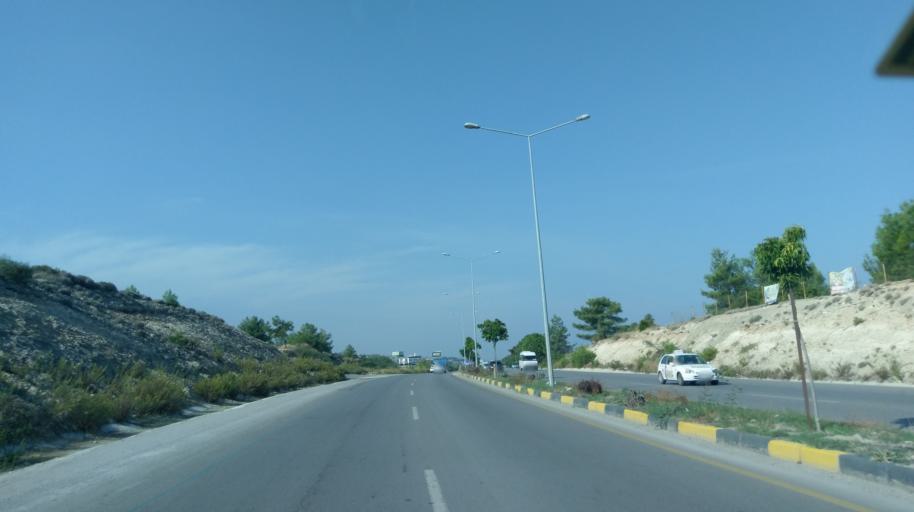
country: CY
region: Keryneia
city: Kyrenia
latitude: 35.3291
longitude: 33.2821
